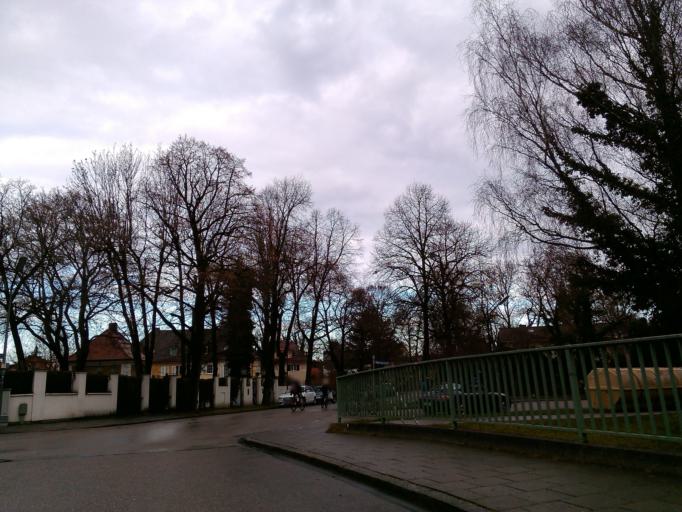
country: DE
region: Bavaria
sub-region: Upper Bavaria
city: Pasing
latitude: 48.1563
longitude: 11.4620
